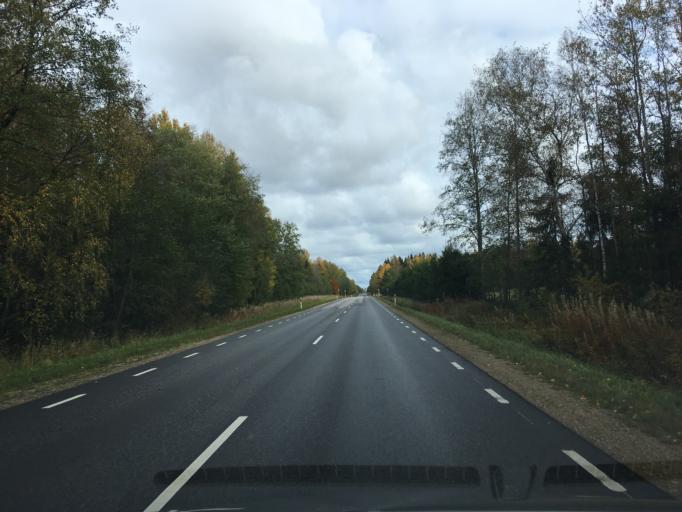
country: EE
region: Harju
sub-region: Anija vald
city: Kehra
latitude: 59.2319
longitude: 25.2822
